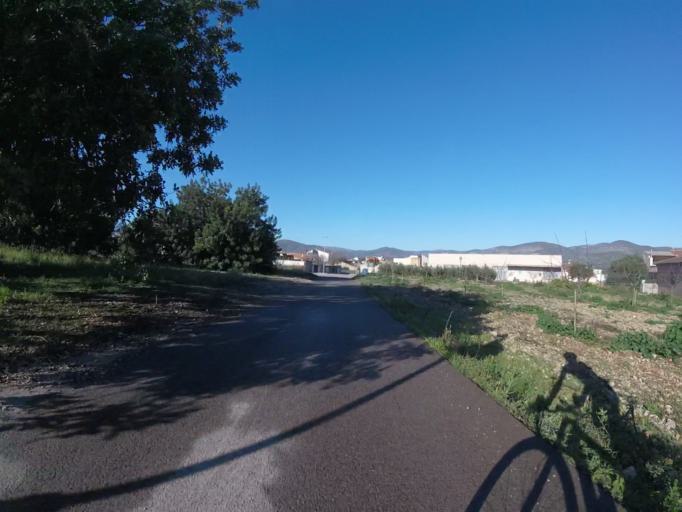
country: ES
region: Valencia
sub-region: Provincia de Castello
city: Santa Magdalena de Pulpis
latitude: 40.3558
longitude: 0.3055
